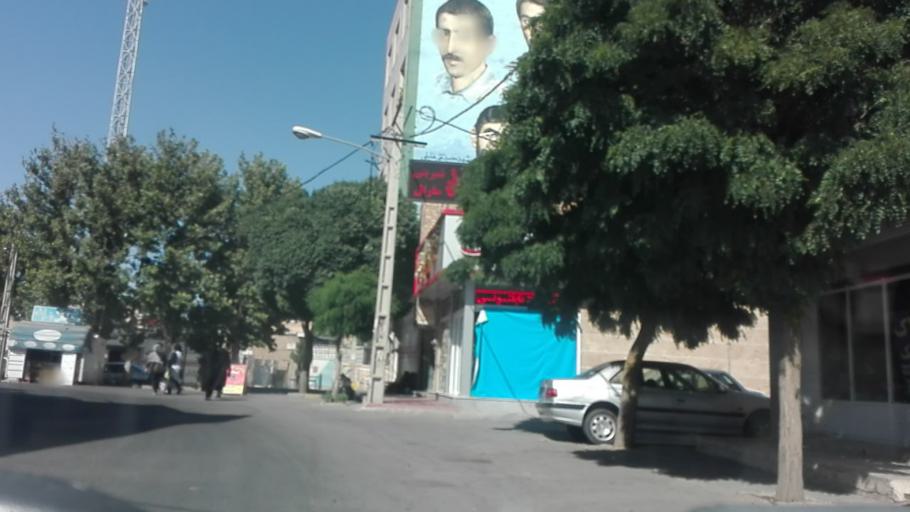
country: IR
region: Tehran
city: Shahriar
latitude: 35.6064
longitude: 51.0667
